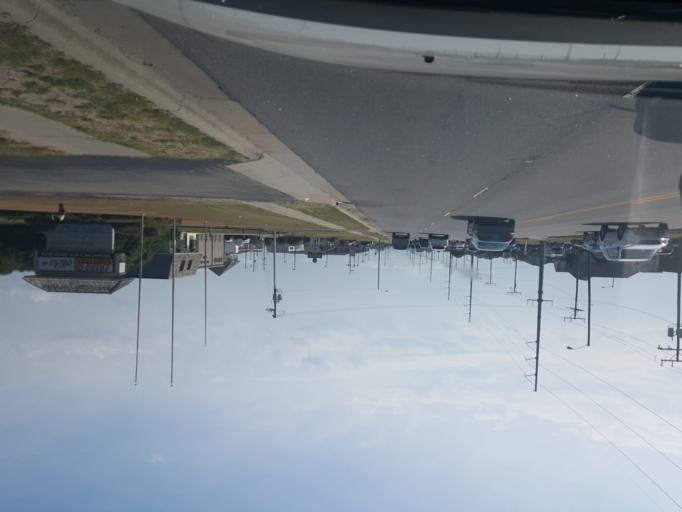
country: US
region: North Carolina
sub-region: Dare County
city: Kill Devil Hills
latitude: 36.0505
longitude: -75.6835
